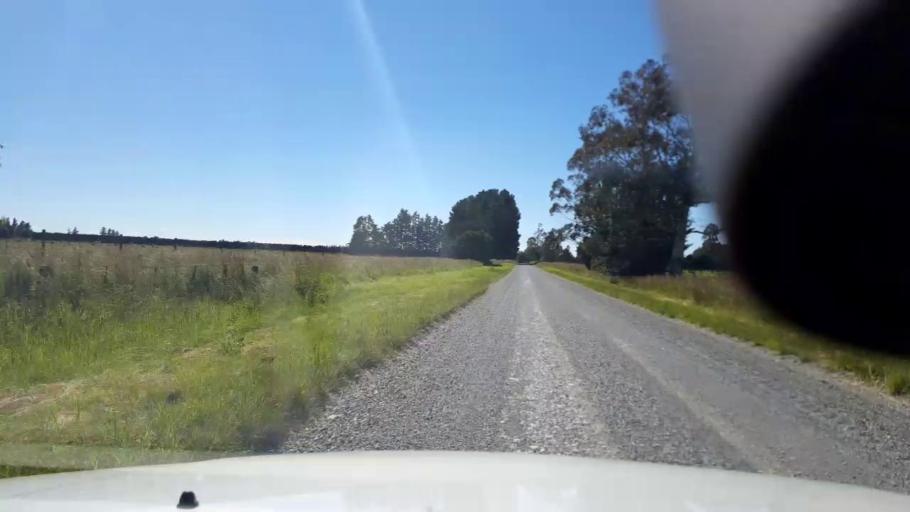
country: NZ
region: Canterbury
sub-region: Timaru District
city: Pleasant Point
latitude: -43.9775
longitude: 171.2712
